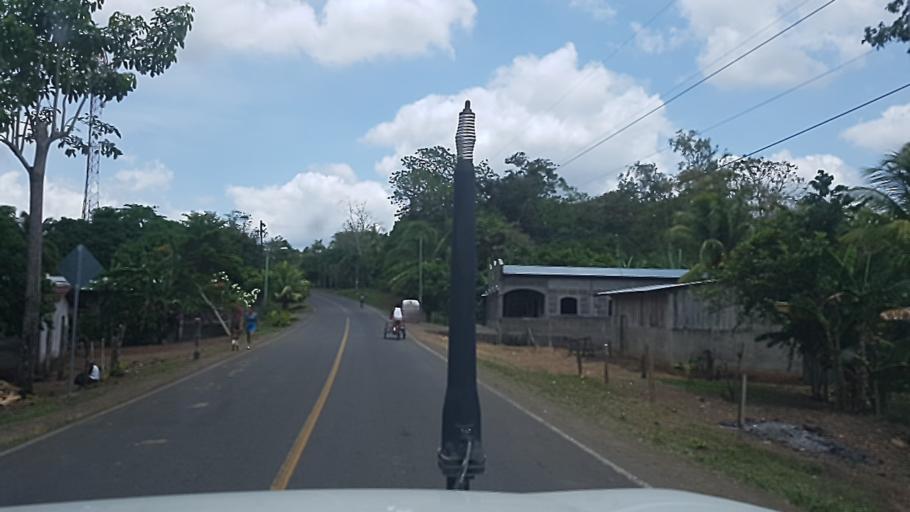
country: NI
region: Atlantico Sur
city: Muelle de los Bueyes
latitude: 11.9218
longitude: -84.6506
